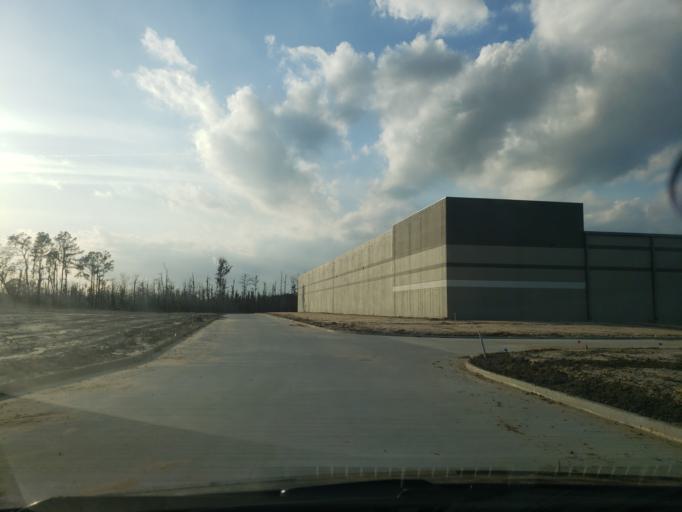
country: US
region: Georgia
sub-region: Chatham County
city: Bloomingdale
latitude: 32.1597
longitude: -81.2758
